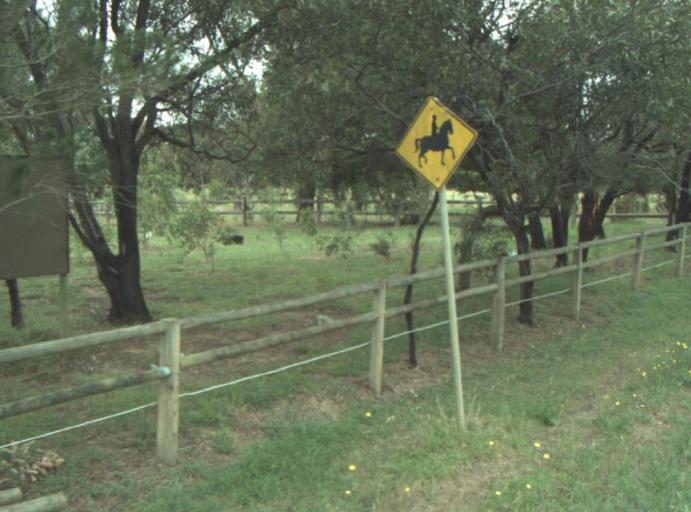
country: AU
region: Victoria
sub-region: Greater Geelong
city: Breakwater
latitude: -38.2032
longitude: 144.4151
